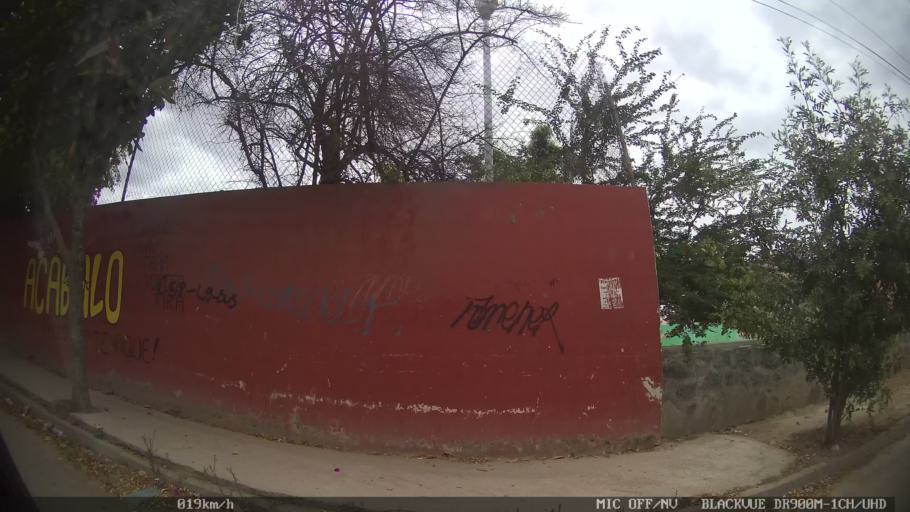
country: MX
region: Jalisco
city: Tonala
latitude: 20.6445
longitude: -103.2515
